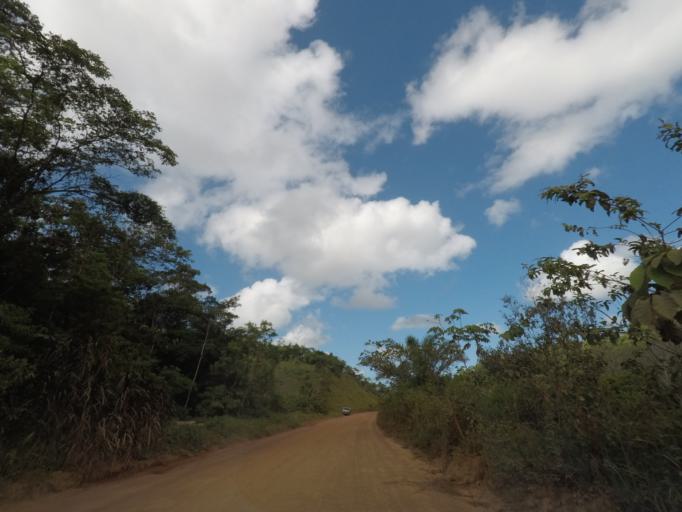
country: BR
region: Bahia
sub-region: Itacare
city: Itacare
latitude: -14.2209
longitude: -39.0757
